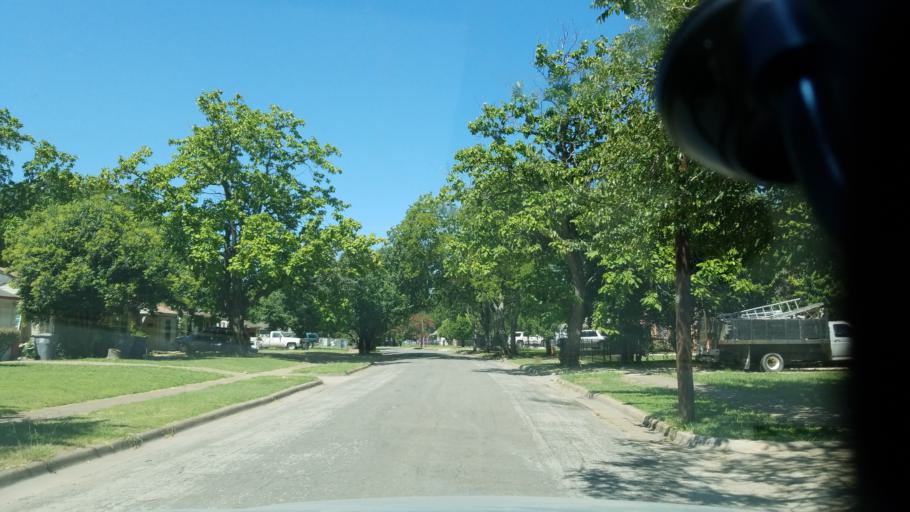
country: US
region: Texas
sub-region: Dallas County
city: Cockrell Hill
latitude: 32.7114
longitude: -96.8238
